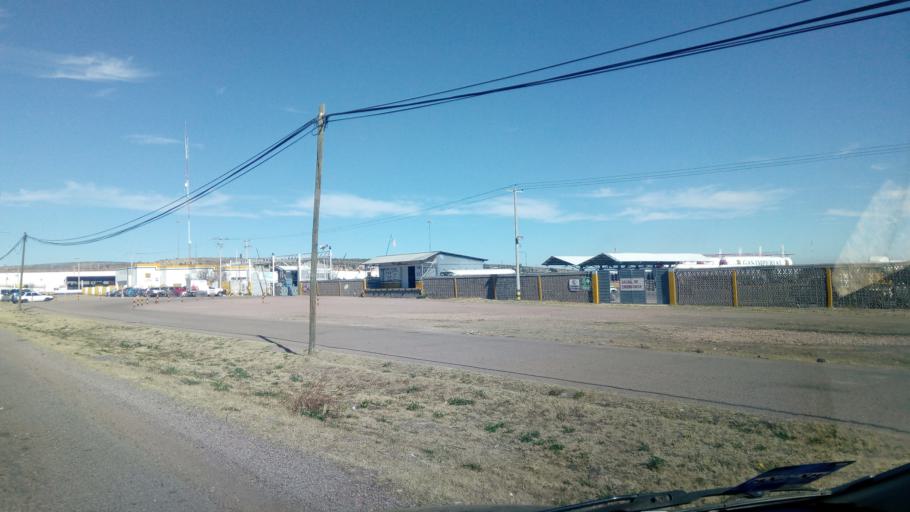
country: MX
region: Durango
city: Victoria de Durango
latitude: 24.0928
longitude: -104.5723
